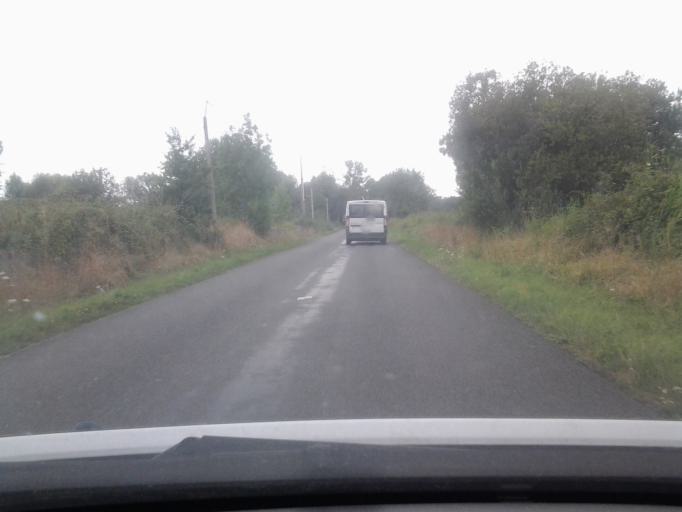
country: FR
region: Pays de la Loire
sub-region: Departement de la Vendee
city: La Tranche-sur-Mer
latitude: 46.3874
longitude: -1.4596
